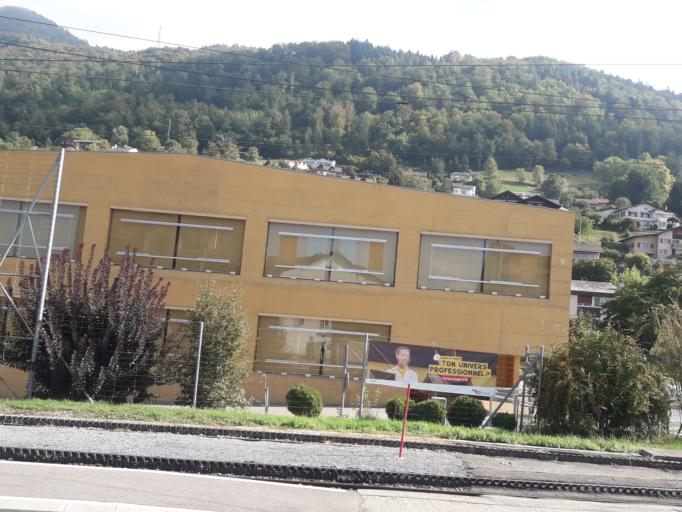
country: CH
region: Vaud
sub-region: Riviera-Pays-d'Enhaut District
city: Blonay
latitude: 46.4658
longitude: 6.8958
